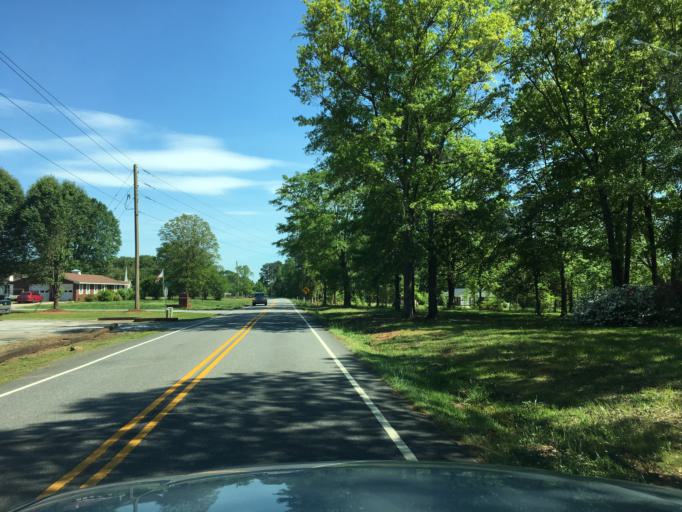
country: US
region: South Carolina
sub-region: Spartanburg County
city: Fairforest
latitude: 34.9732
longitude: -82.0529
